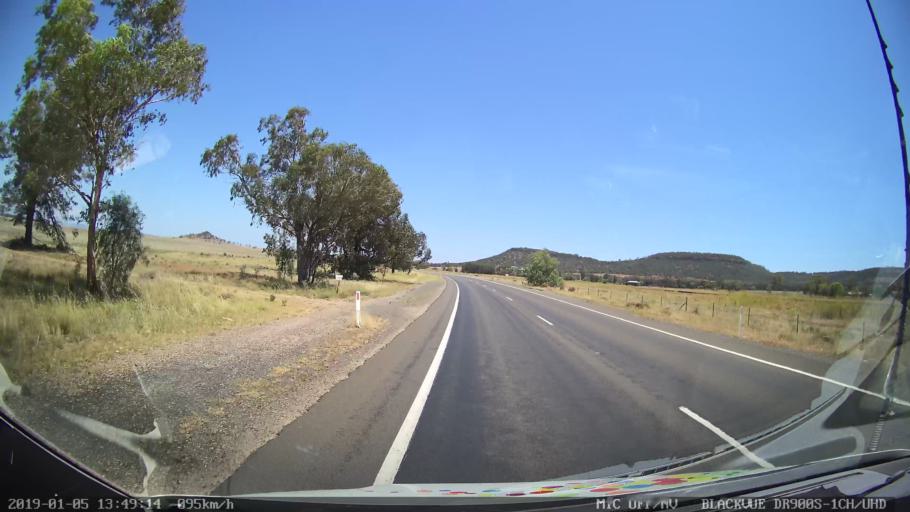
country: AU
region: New South Wales
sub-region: Gunnedah
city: Gunnedah
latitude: -31.0130
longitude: 150.2739
